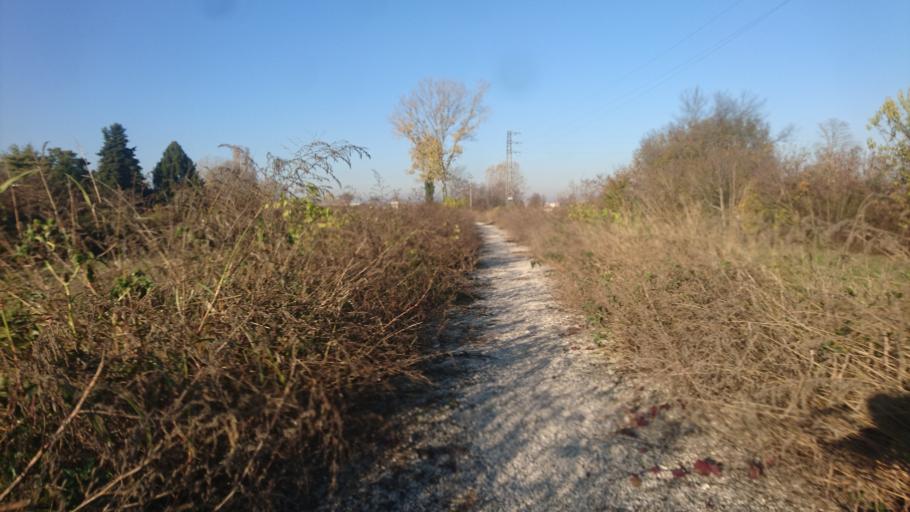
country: IT
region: Veneto
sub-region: Provincia di Padova
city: Villaguattera
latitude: 45.4348
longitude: 11.8280
